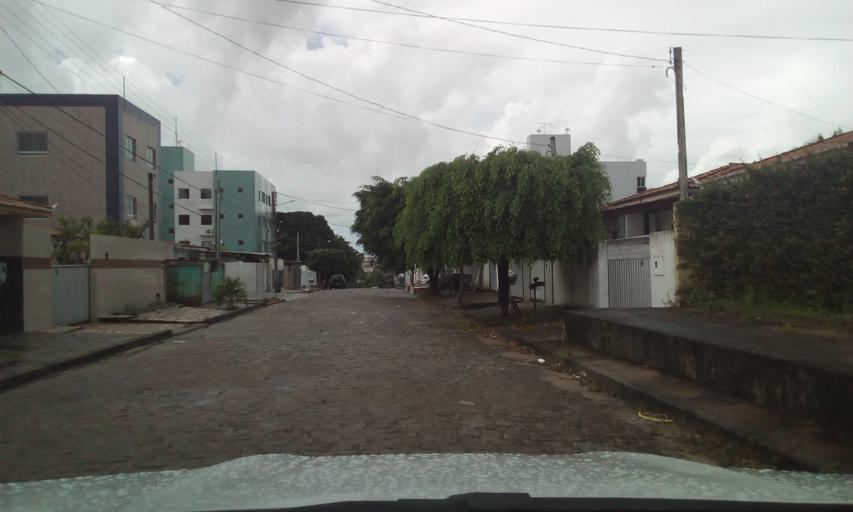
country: BR
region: Paraiba
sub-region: Joao Pessoa
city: Joao Pessoa
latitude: -7.1675
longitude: -34.8488
